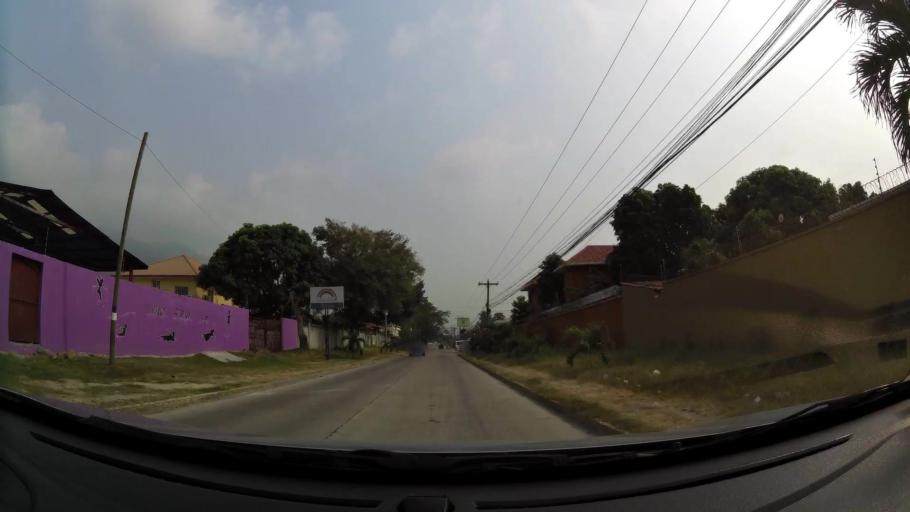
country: HN
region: Cortes
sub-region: San Pedro Sula
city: Pena Blanca
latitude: 15.5369
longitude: -88.0329
